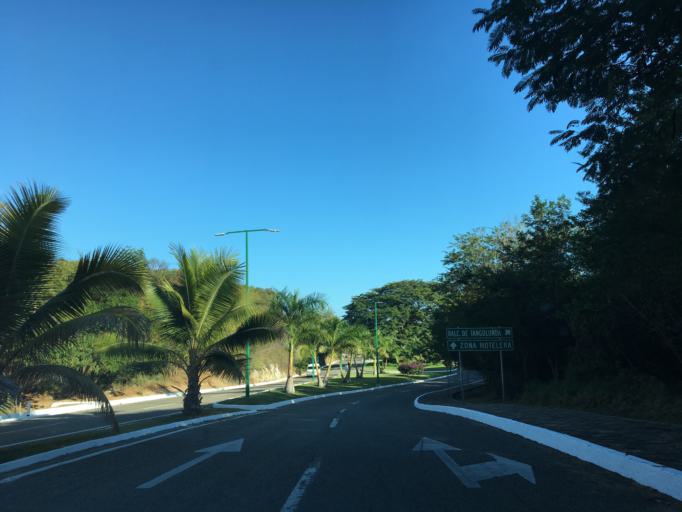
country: MX
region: Oaxaca
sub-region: Santa Maria Huatulco
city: Crucecita
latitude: 15.7760
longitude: -96.0885
